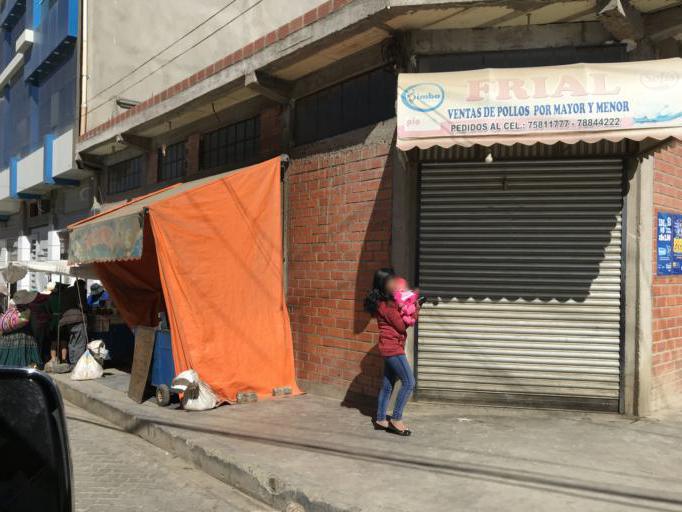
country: BO
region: La Paz
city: La Paz
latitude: -16.4904
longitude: -68.2110
